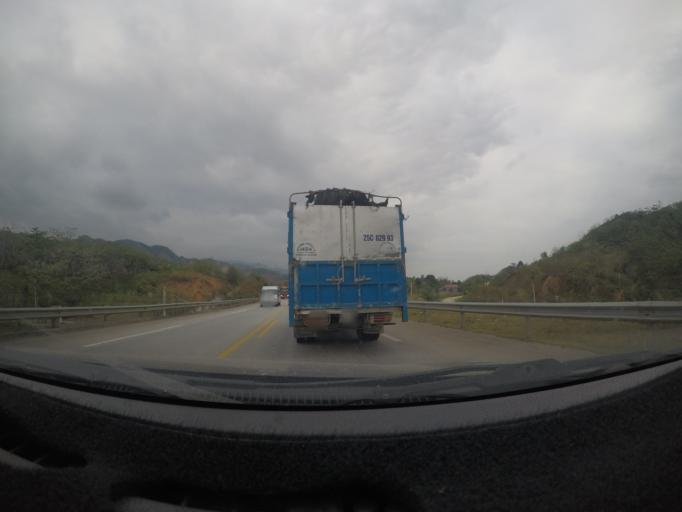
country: VN
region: Lao Cai
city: Thi Tran Pho Rang
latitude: 22.0863
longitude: 104.4452
